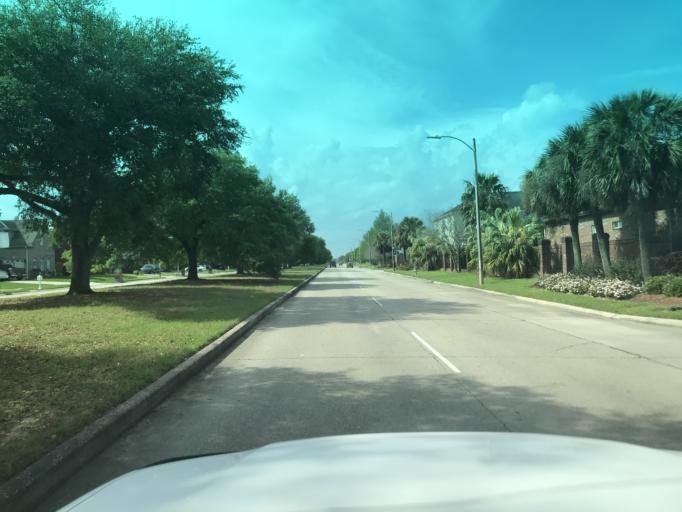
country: US
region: Louisiana
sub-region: Saint Bernard Parish
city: Chalmette
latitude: 30.0358
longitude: -89.9524
